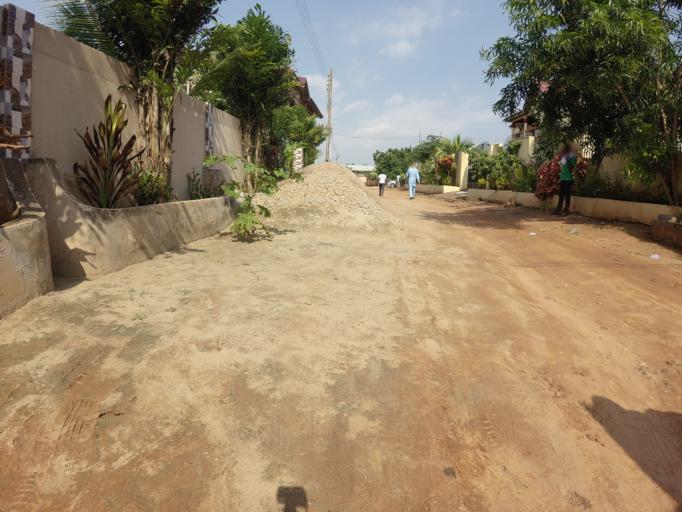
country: GH
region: Greater Accra
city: Gbawe
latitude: 5.6232
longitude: -0.3108
